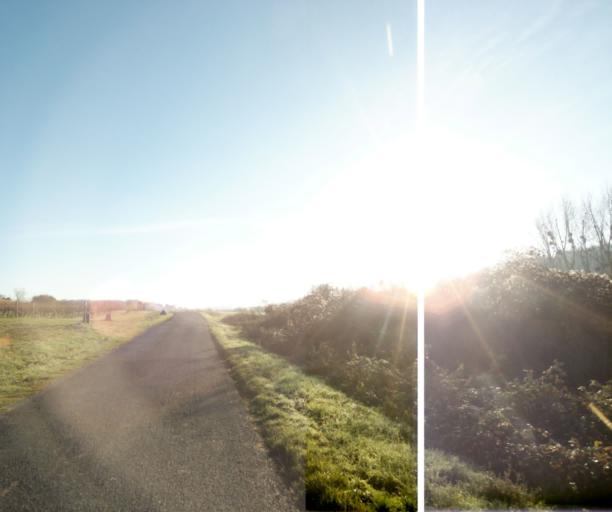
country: FR
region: Poitou-Charentes
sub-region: Departement de la Charente-Maritime
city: Cherac
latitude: 45.6996
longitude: -0.4173
